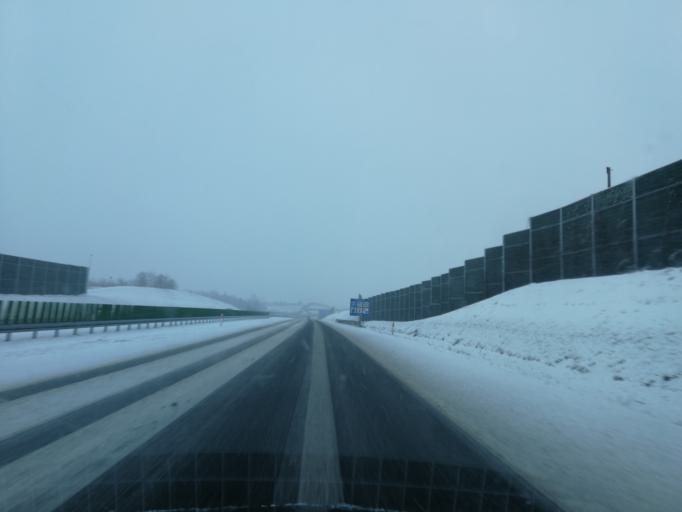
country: PL
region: Silesian Voivodeship
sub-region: Powiat wodzislawski
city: Polomia
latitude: 49.9887
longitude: 18.5650
